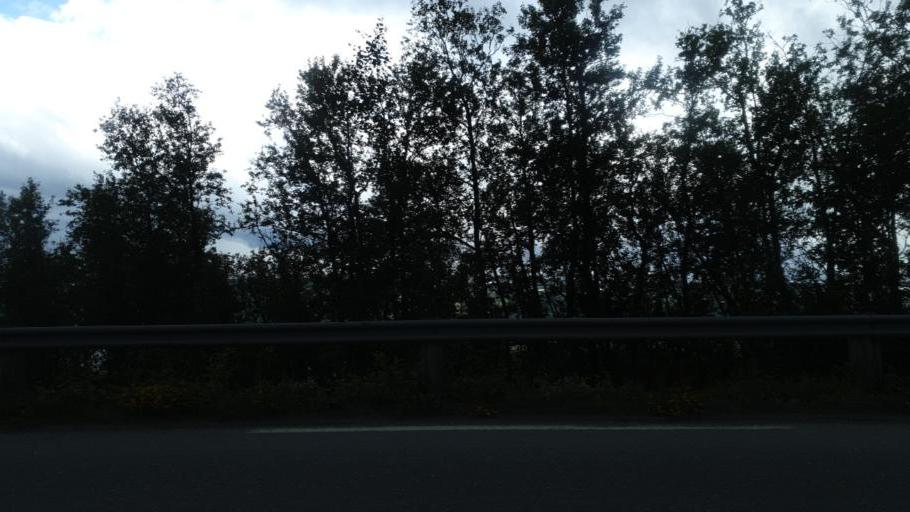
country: NO
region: Oppland
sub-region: Vestre Slidre
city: Slidre
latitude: 61.2513
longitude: 8.8828
